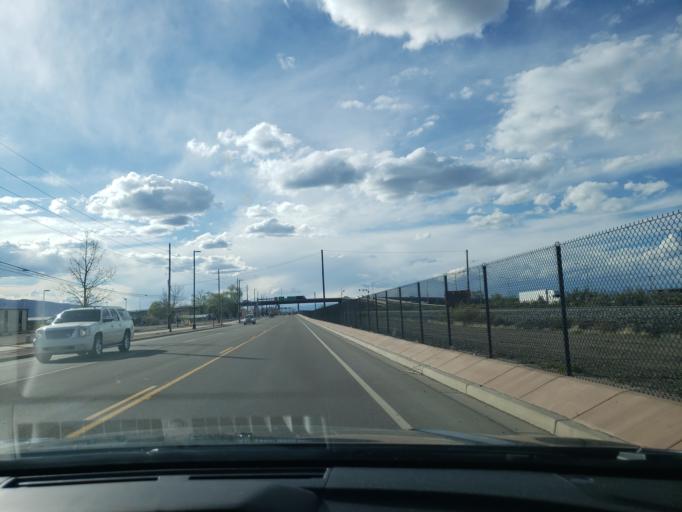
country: US
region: Colorado
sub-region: Mesa County
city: Redlands
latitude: 39.0892
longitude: -108.6056
